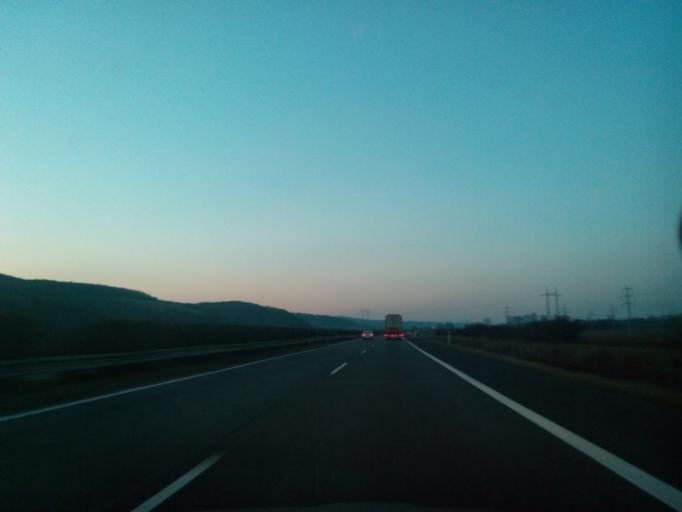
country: SK
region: Presovsky
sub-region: Okres Presov
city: Presov
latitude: 48.8808
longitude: 21.2511
